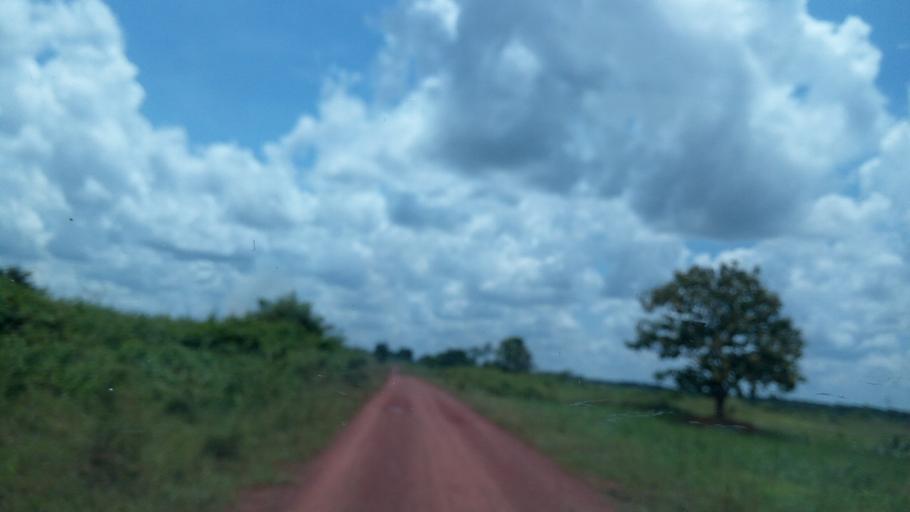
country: CD
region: Equateur
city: Libenge
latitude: 3.7732
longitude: 18.9402
